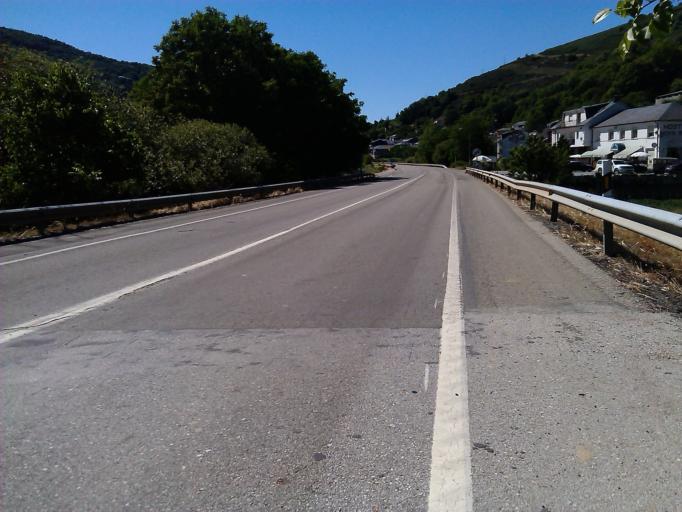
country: ES
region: Castille and Leon
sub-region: Provincia de Leon
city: Trabadelo
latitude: 42.6468
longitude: -6.8761
